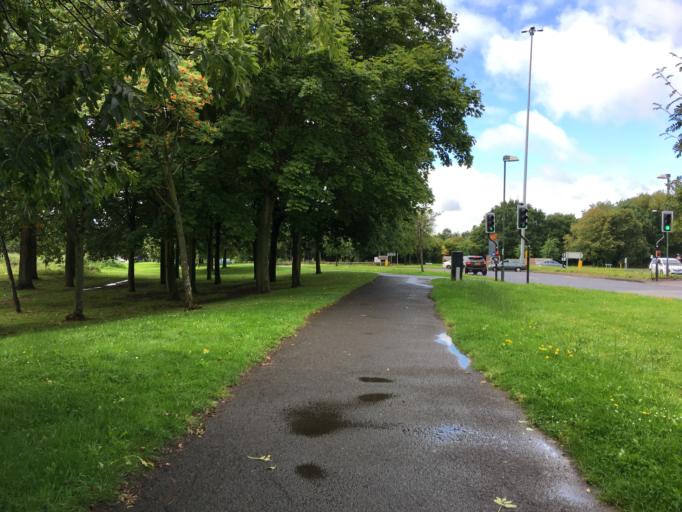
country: GB
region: England
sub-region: Coventry
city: Coventry
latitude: 52.3901
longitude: -1.5548
